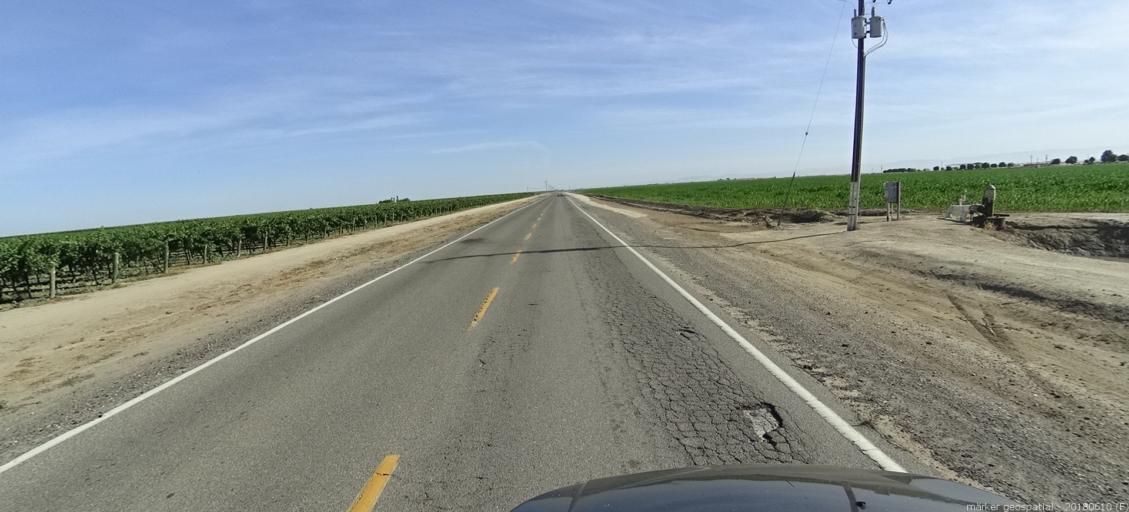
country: US
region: California
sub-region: Madera County
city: Fairmead
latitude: 36.9275
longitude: -120.2556
